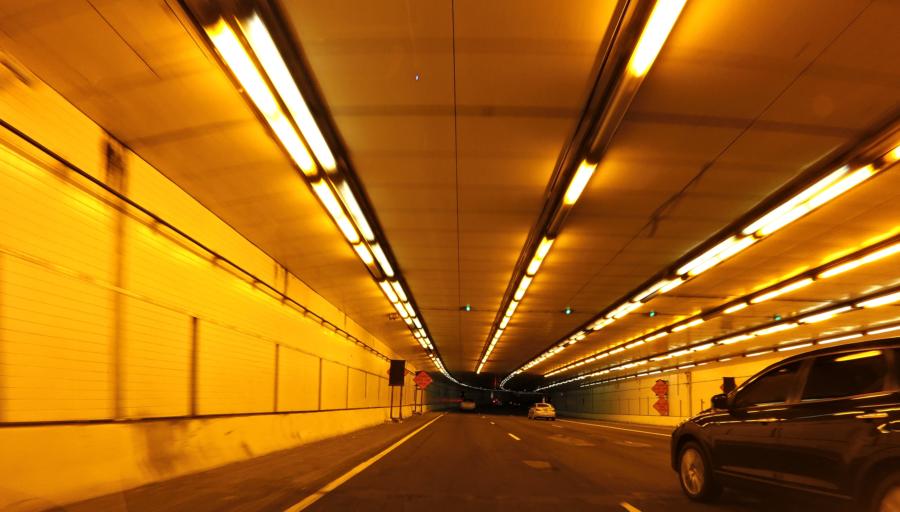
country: US
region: Washington, D.C.
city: Washington, D.C.
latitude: 38.8862
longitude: -77.0129
